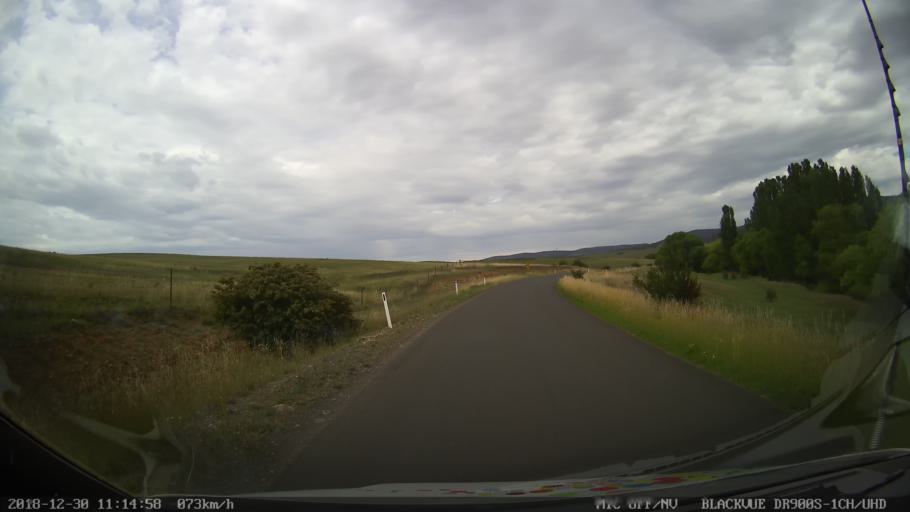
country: AU
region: New South Wales
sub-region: Snowy River
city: Jindabyne
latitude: -36.5414
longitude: 148.7271
